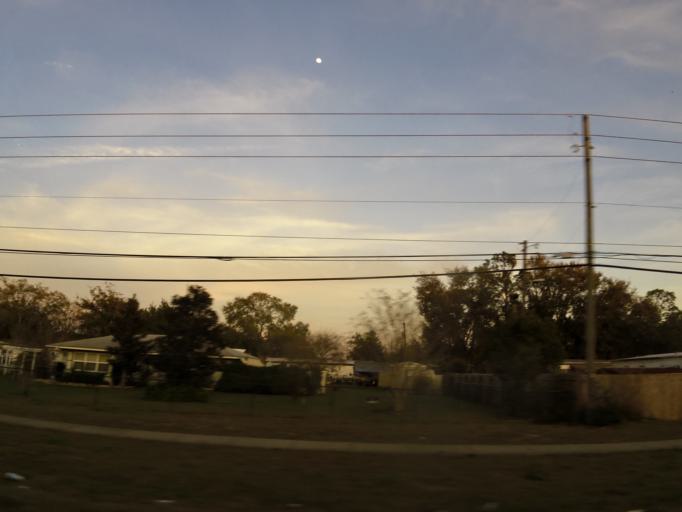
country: US
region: Florida
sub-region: Volusia County
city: North DeLand
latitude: 29.0746
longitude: -81.3047
